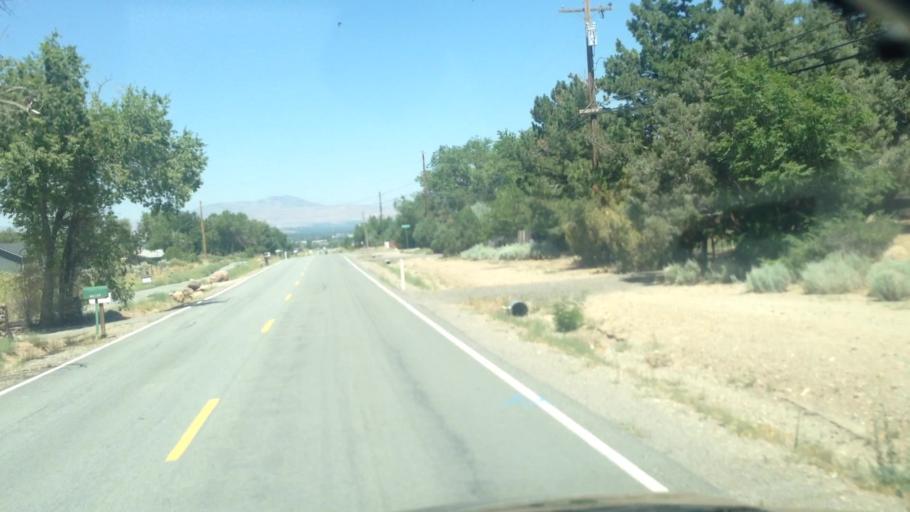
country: US
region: Nevada
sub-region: Storey County
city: Virginia City
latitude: 39.3838
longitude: -119.7238
